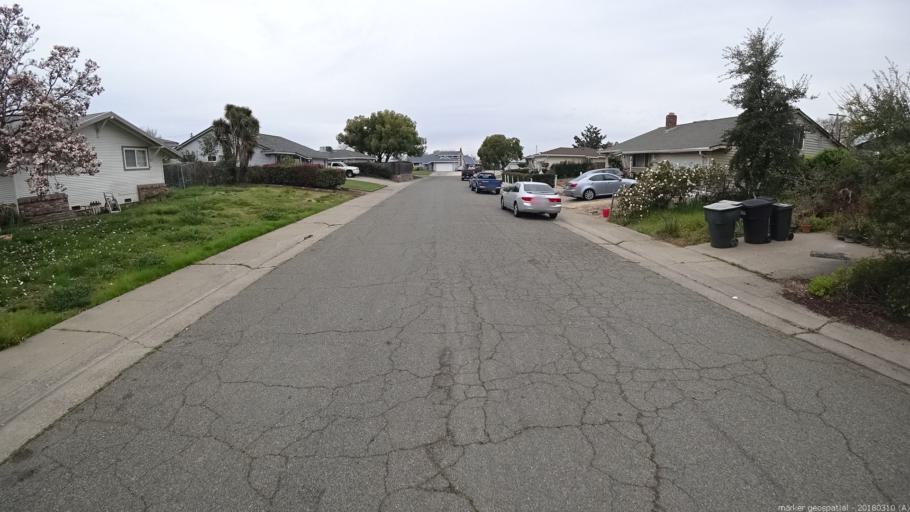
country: US
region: California
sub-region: Sacramento County
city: Vineyard
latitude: 38.4808
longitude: -121.3772
